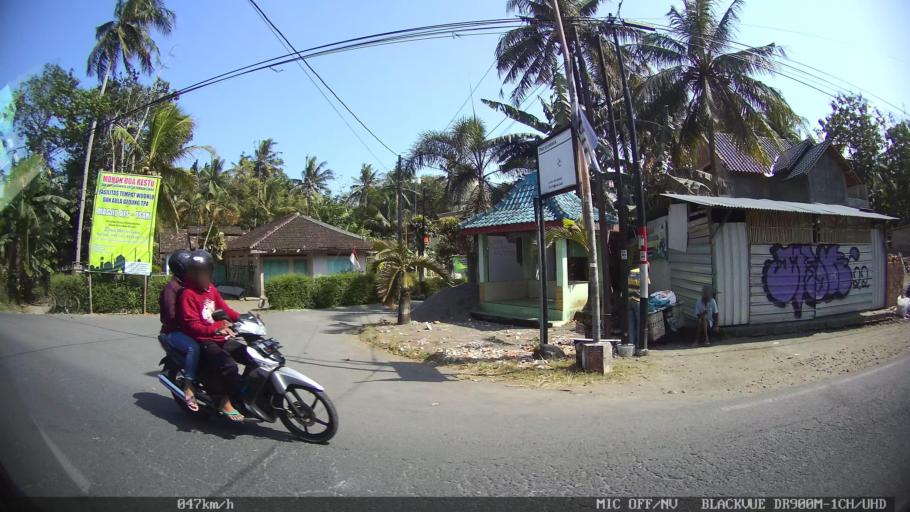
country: ID
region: Daerah Istimewa Yogyakarta
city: Srandakan
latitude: -7.9479
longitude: 110.2229
